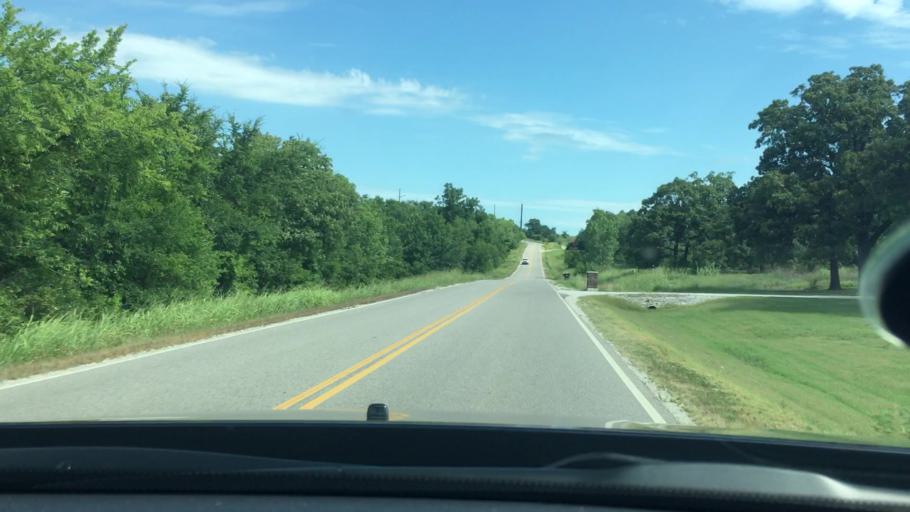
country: US
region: Oklahoma
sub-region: Pontotoc County
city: Ada
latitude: 34.7680
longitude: -96.5821
